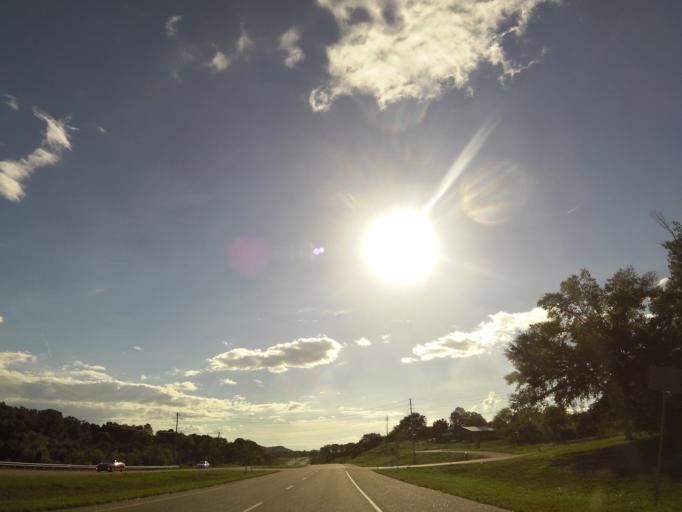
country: US
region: Tennessee
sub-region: Cocke County
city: Newport
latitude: 35.9890
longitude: -83.1322
